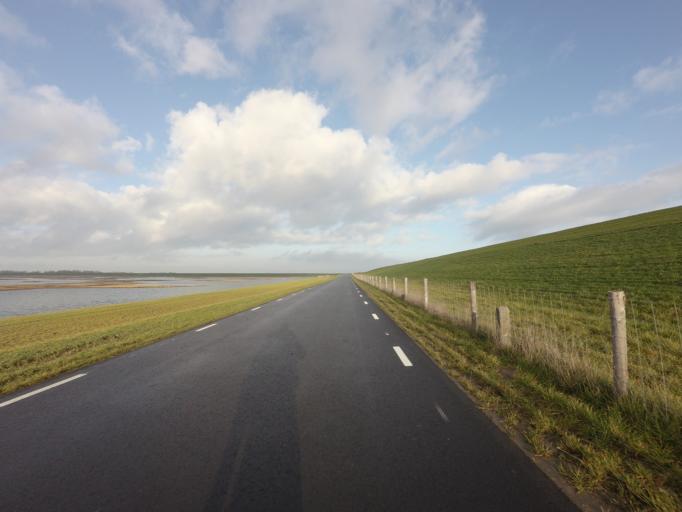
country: NL
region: North Holland
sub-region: Gemeente Texel
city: Den Burg
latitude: 53.1225
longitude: 4.8990
